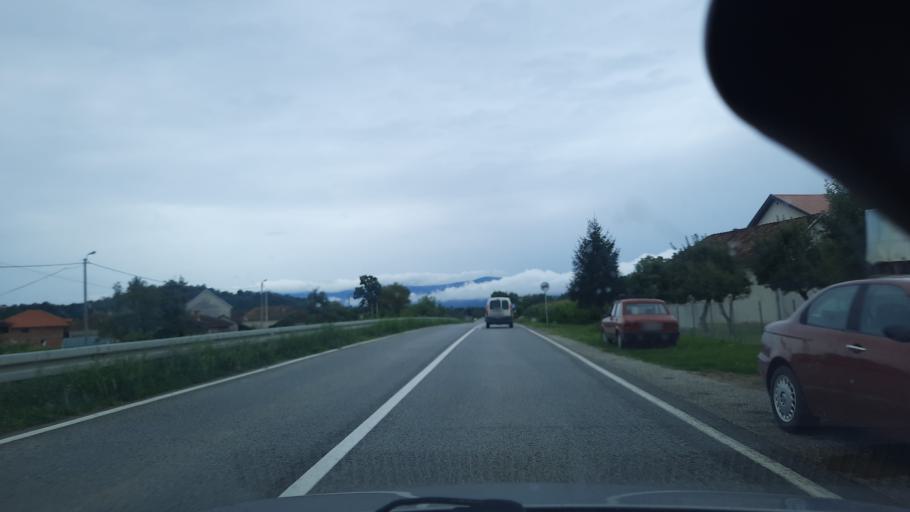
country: RS
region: Central Serbia
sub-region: Raski Okrug
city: Kraljevo
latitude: 43.7393
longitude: 20.8037
